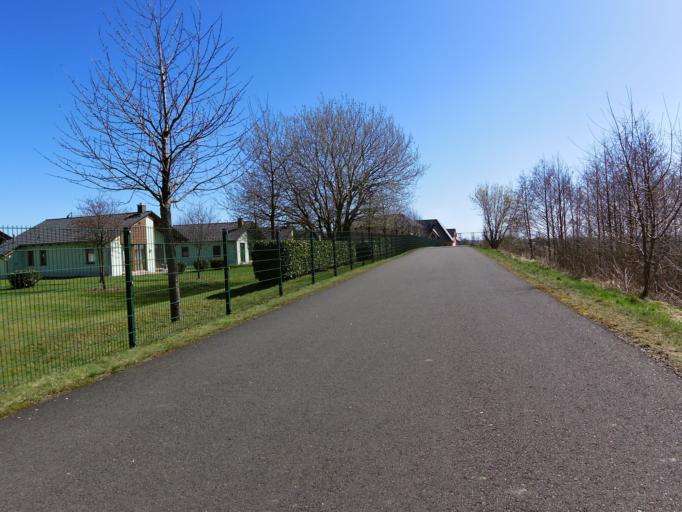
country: DE
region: Saxony
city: Markkleeberg
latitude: 51.2620
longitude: 12.4264
